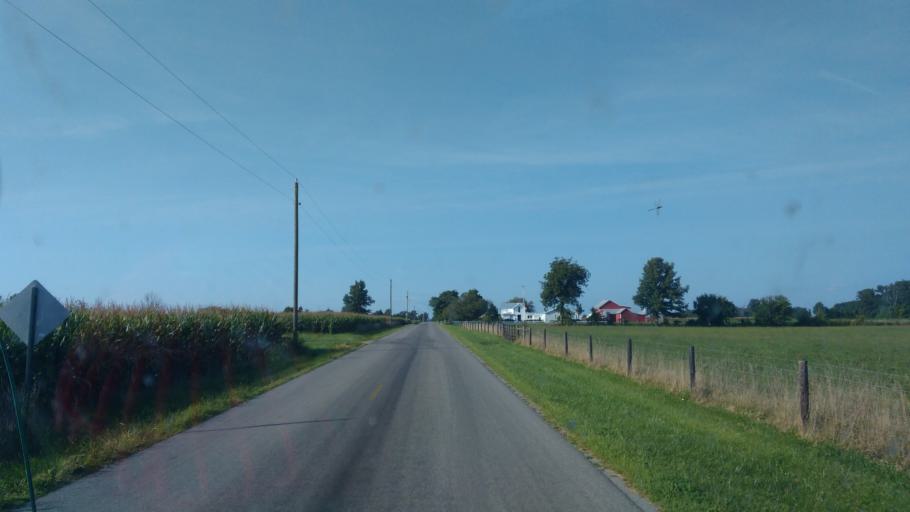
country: US
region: Ohio
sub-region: Hardin County
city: Forest
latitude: 40.8339
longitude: -83.4189
